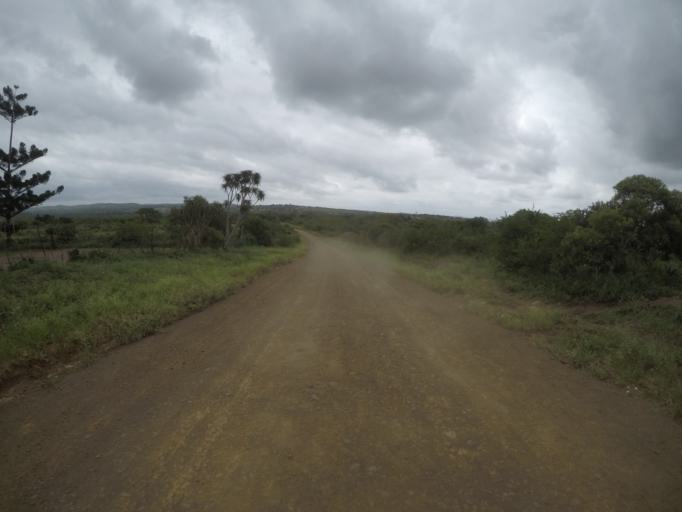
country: ZA
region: KwaZulu-Natal
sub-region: uThungulu District Municipality
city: Empangeni
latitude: -28.5852
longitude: 31.8618
